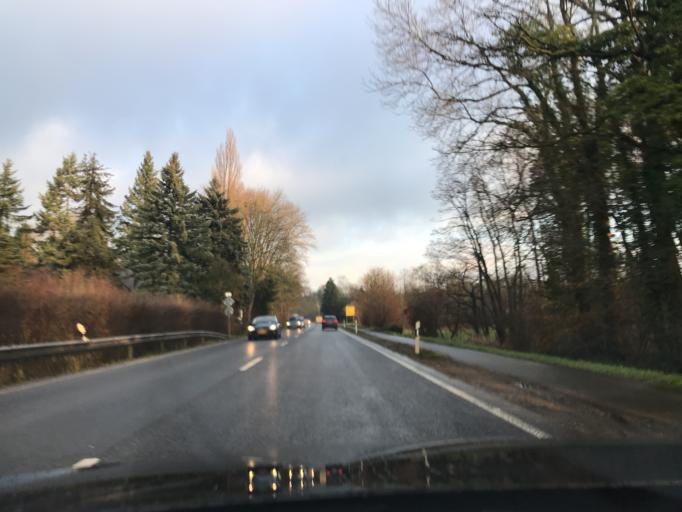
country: DE
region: North Rhine-Westphalia
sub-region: Regierungsbezirk Dusseldorf
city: Rheurdt
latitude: 51.3999
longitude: 6.4982
